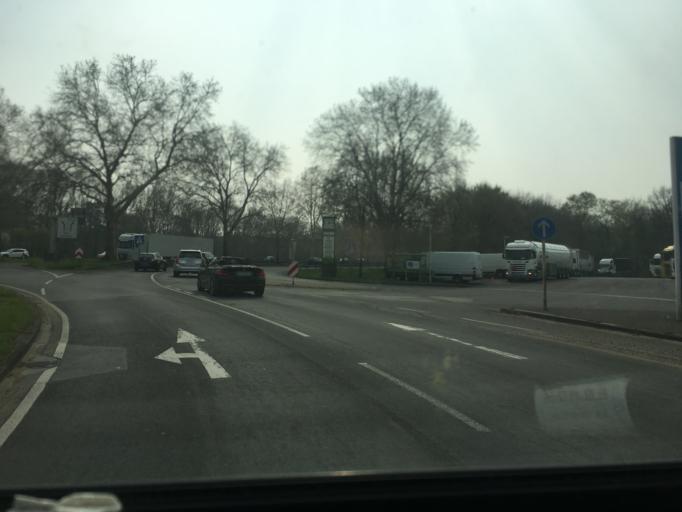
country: DE
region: North Rhine-Westphalia
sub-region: Regierungsbezirk Koln
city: Bayenthal
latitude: 50.8922
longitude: 6.9667
